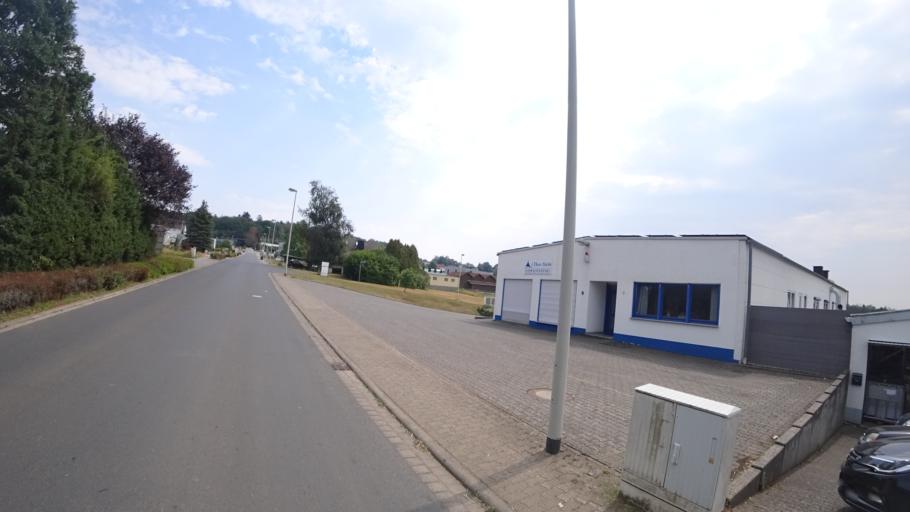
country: DE
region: Rheinland-Pfalz
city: Hillscheid
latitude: 50.4137
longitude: 7.6869
